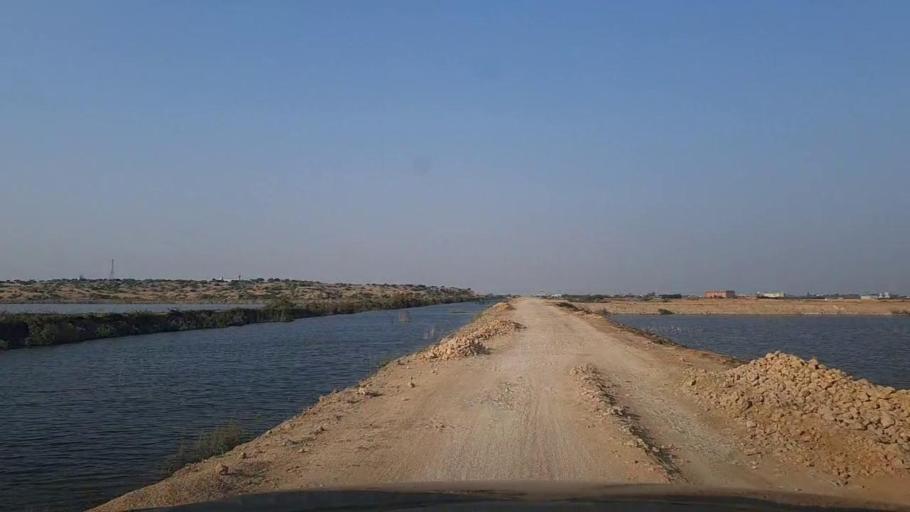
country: PK
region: Sindh
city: Thatta
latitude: 24.7373
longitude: 67.9064
